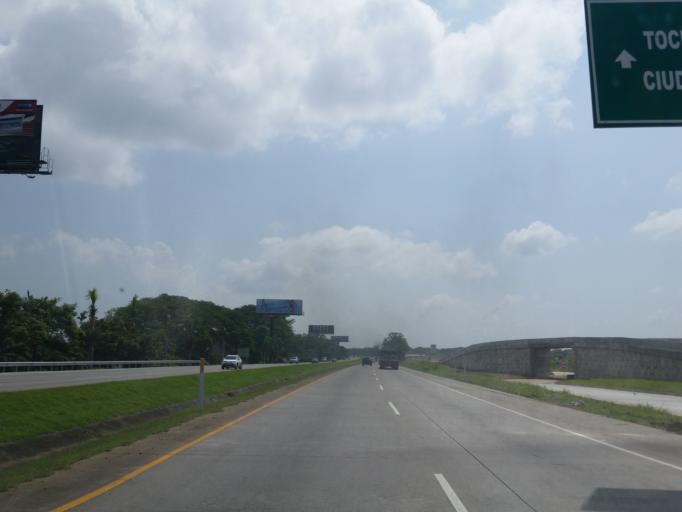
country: PA
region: Panama
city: San Miguelito
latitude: 9.0298
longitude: -79.4534
